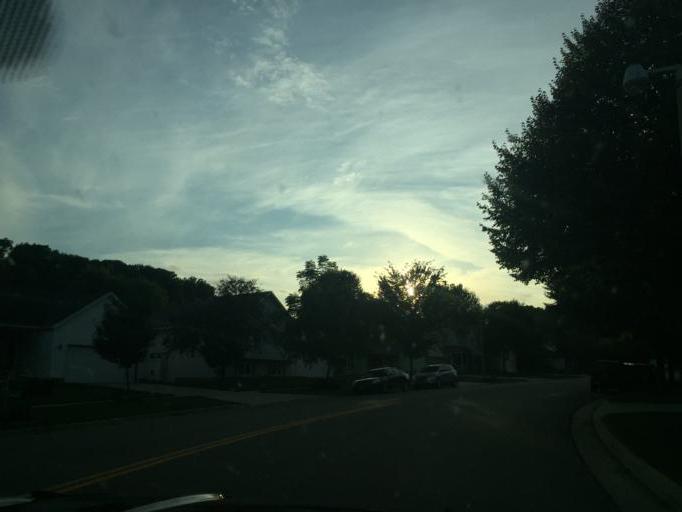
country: US
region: Minnesota
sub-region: Olmsted County
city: Rochester
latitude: 44.0054
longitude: -92.4885
